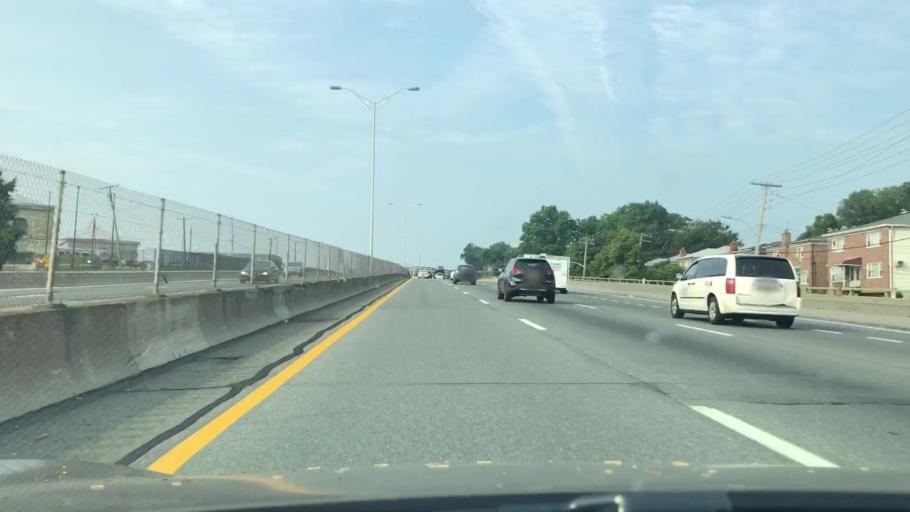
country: US
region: New York
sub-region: Westchester County
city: Yonkers
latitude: 40.9189
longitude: -73.8694
